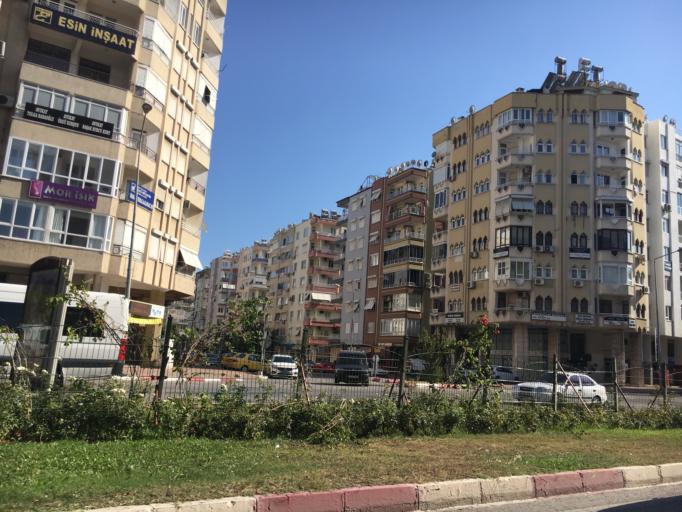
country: TR
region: Antalya
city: Antalya
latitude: 36.8897
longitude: 30.6874
